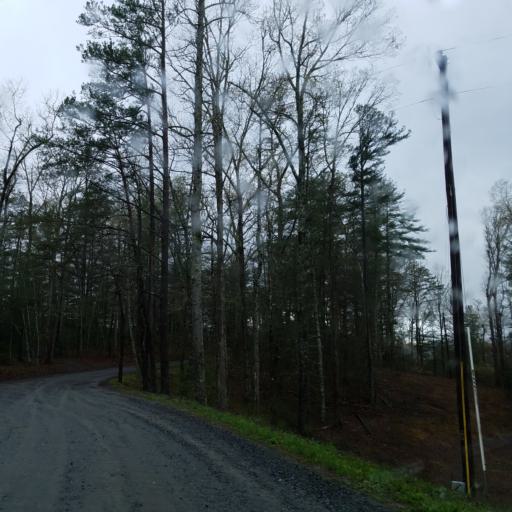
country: US
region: Georgia
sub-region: Fannin County
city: Blue Ridge
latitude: 34.8219
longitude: -84.2326
